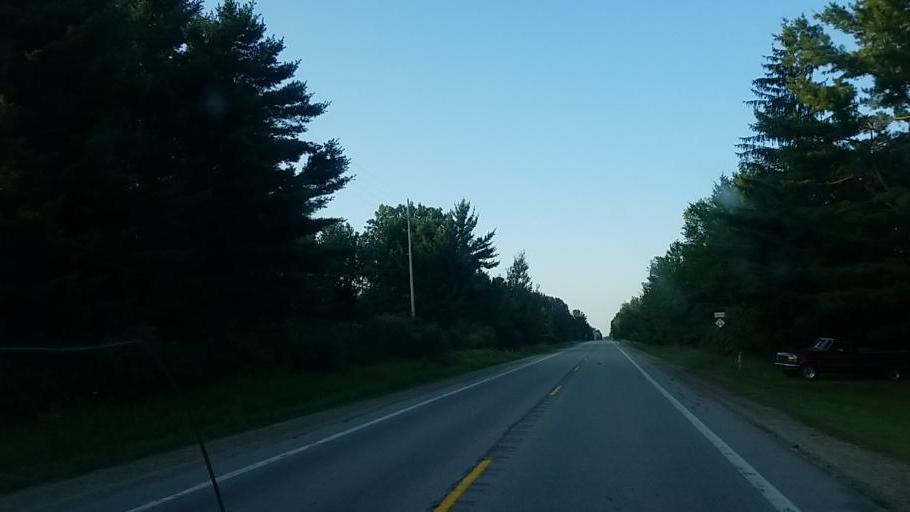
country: US
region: Michigan
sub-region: Isabella County
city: Lake Isabella
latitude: 43.6467
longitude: -85.1462
